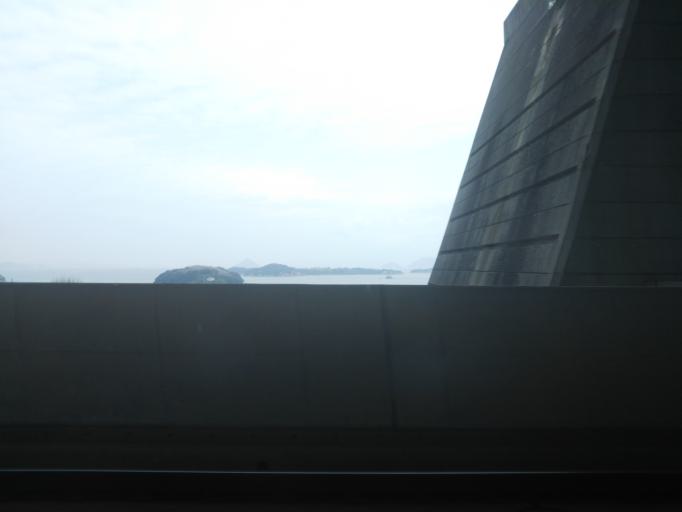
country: JP
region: Kagawa
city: Sakaidecho
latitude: 34.4251
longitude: 133.8045
